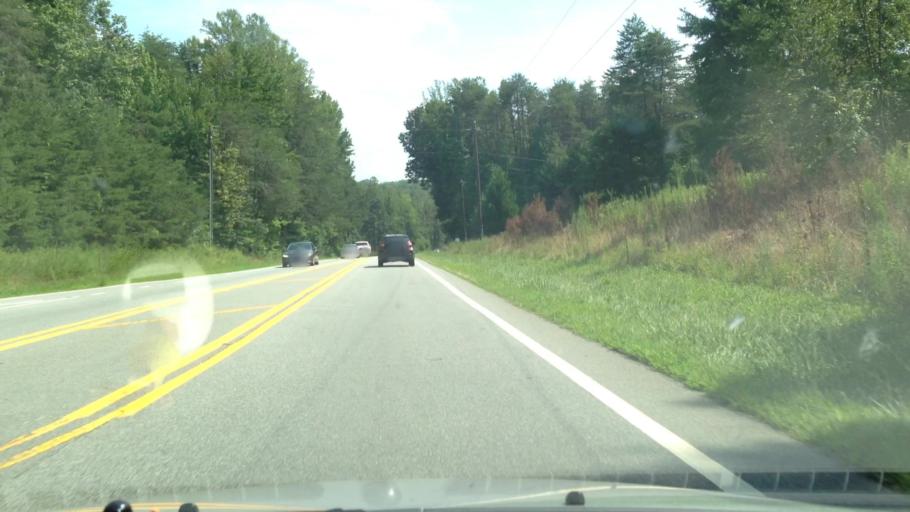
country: US
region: North Carolina
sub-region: Guilford County
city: Oak Ridge
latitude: 36.2033
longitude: -79.9865
